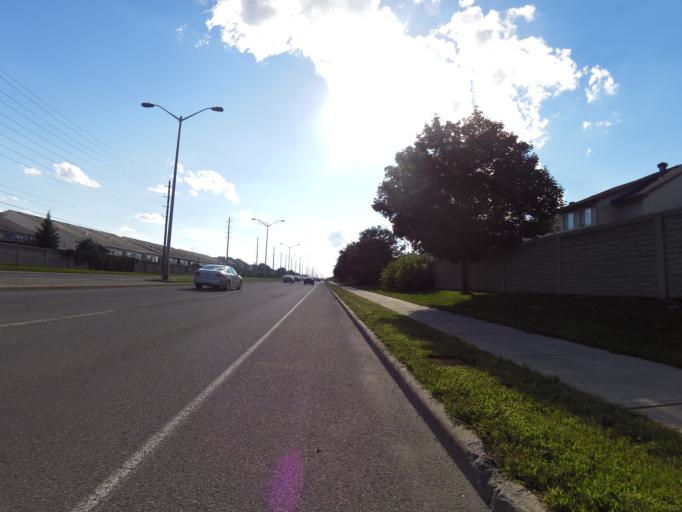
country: CA
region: Ontario
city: Clarence-Rockland
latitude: 45.4688
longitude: -75.4612
